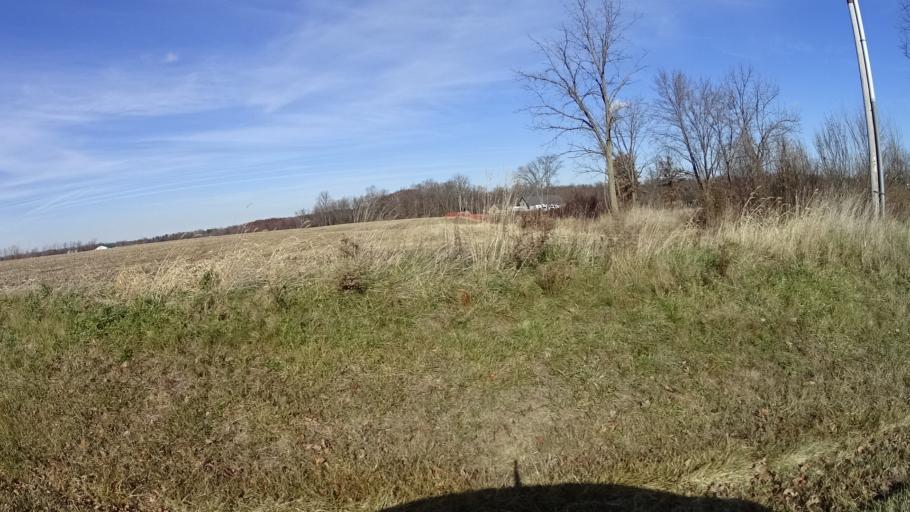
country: US
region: Ohio
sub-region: Lorain County
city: Wellington
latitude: 41.0854
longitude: -82.2498
